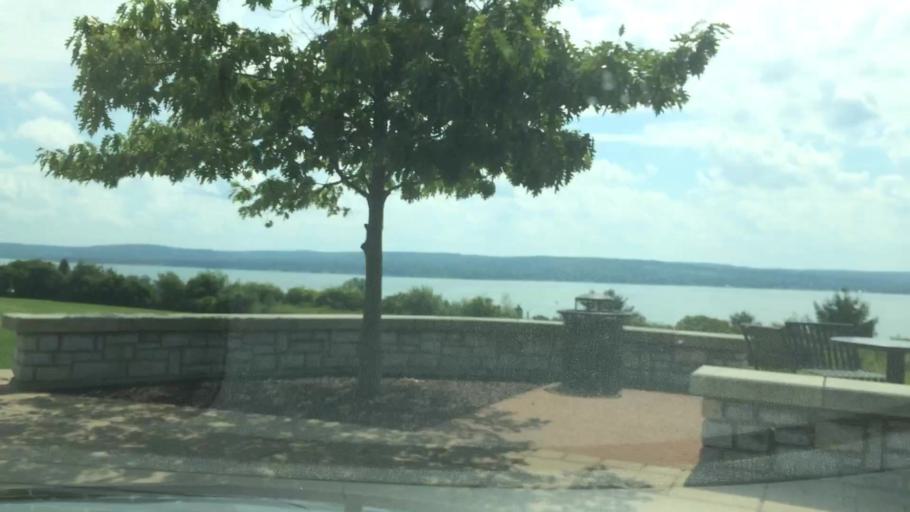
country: US
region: New York
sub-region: Chautauqua County
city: Lakewood
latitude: 42.1342
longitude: -79.3492
